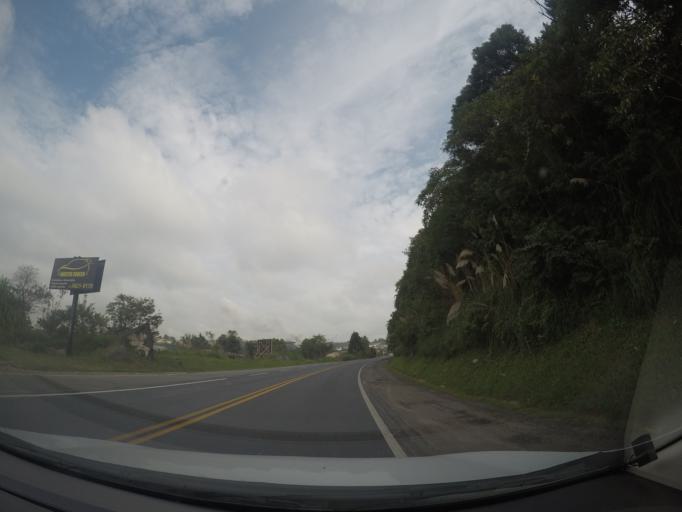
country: BR
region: Parana
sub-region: Colombo
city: Colombo
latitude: -25.3442
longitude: -49.2296
